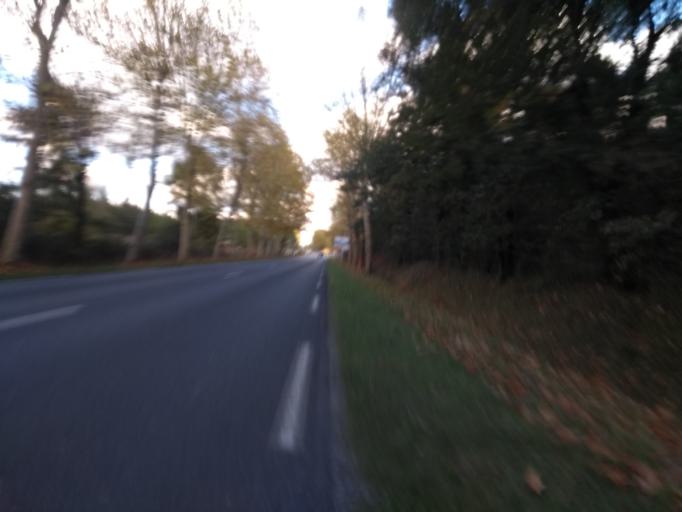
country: FR
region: Aquitaine
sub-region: Departement de la Gironde
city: Saint-Aubin-de-Medoc
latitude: 44.6984
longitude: -0.7081
